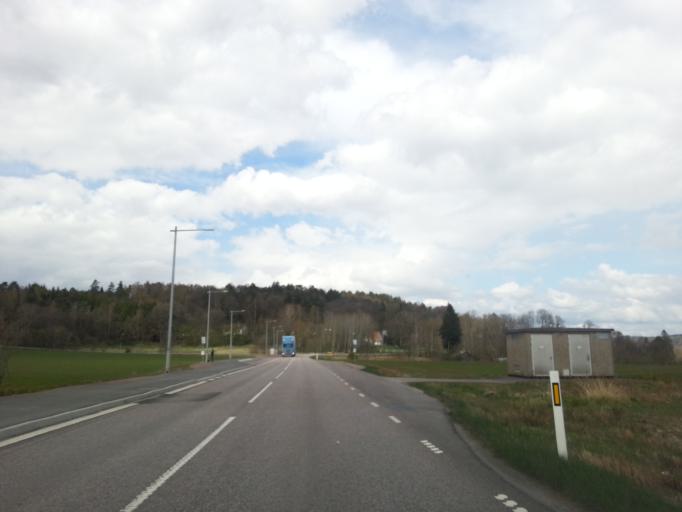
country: SE
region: Vaestra Goetaland
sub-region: Ale Kommun
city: Surte
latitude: 57.8082
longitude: 11.9971
